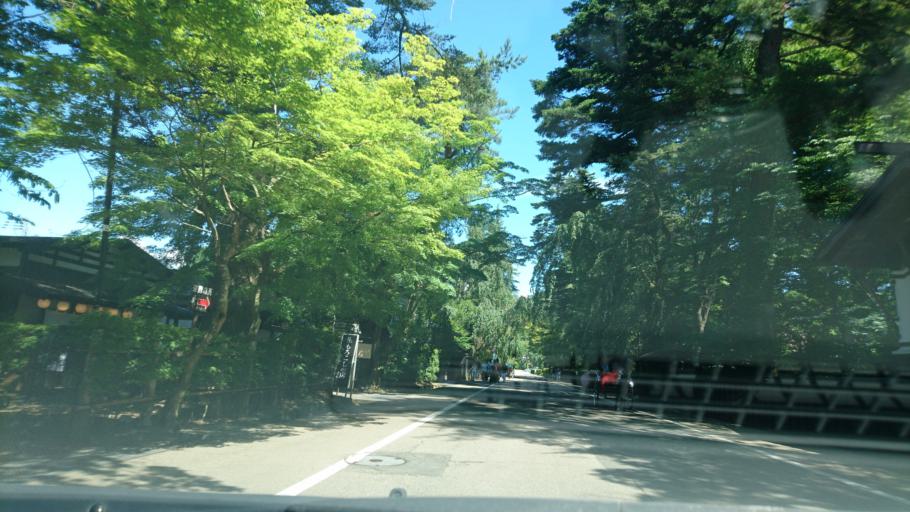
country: JP
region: Akita
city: Kakunodatemachi
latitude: 39.6005
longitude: 140.5614
